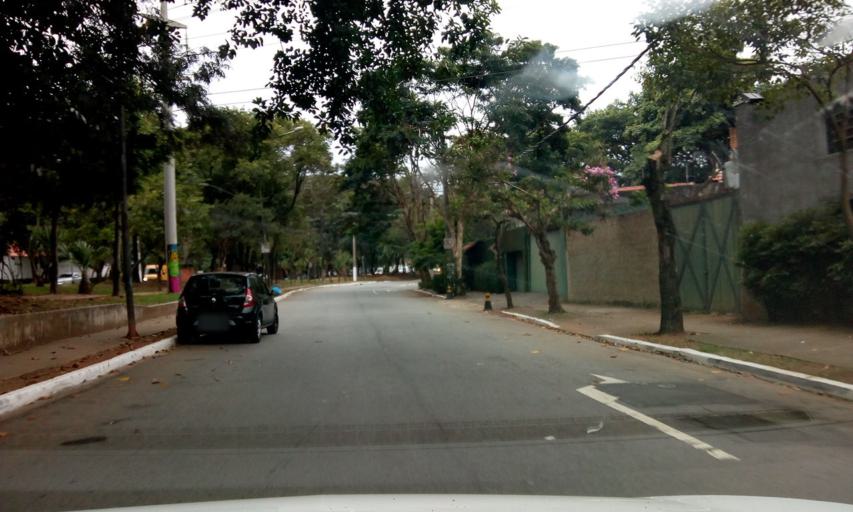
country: BR
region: Sao Paulo
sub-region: Osasco
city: Osasco
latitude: -23.5491
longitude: -46.7168
